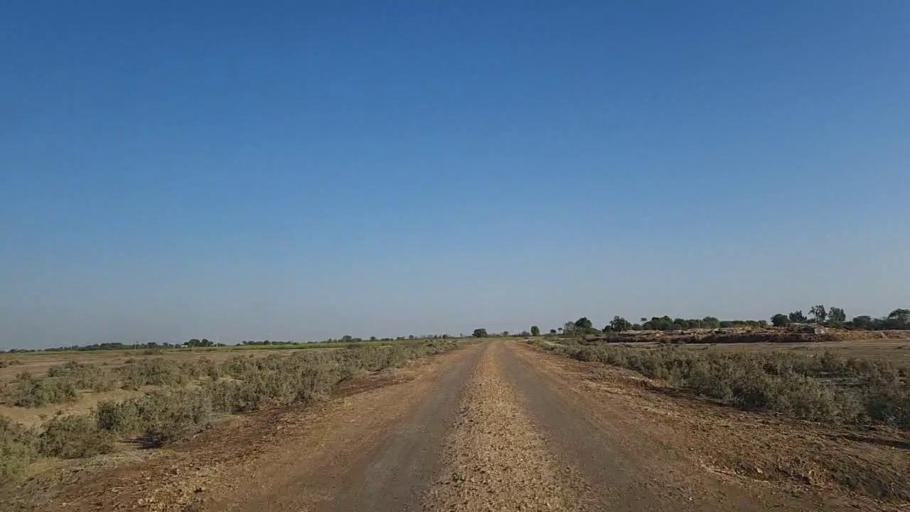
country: PK
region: Sindh
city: Naukot
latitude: 24.9721
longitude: 69.3794
